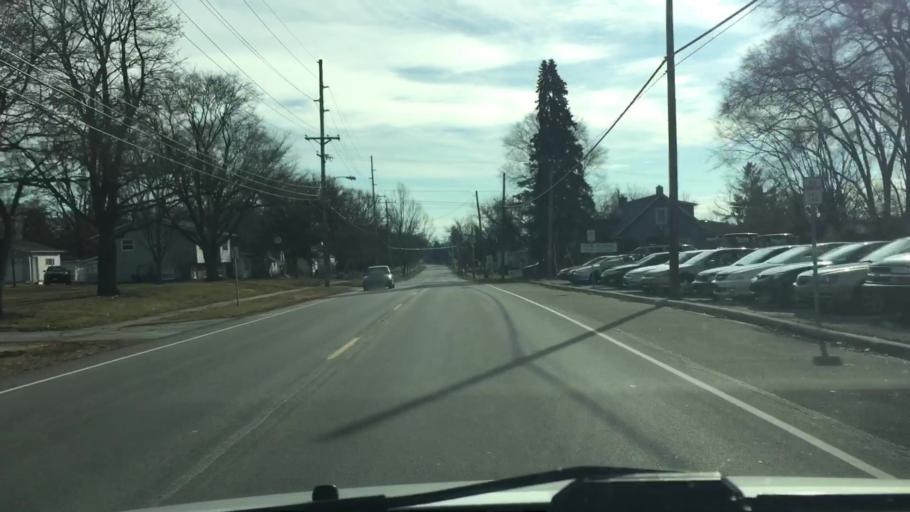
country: US
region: Illinois
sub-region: Kane County
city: Batavia
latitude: 41.8607
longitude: -88.3066
